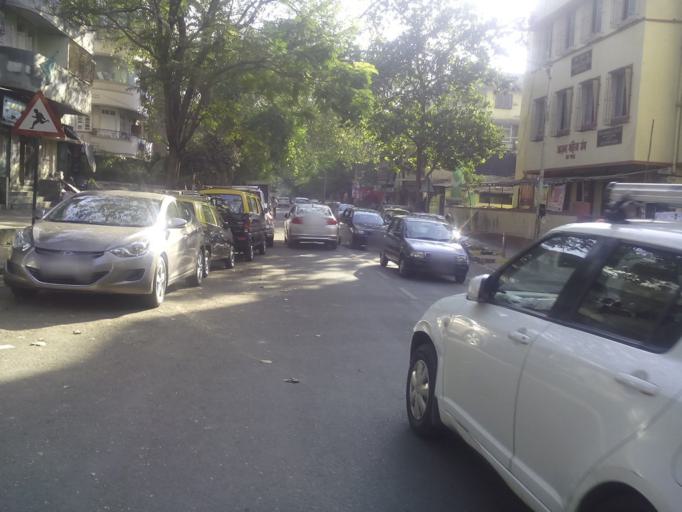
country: IN
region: Maharashtra
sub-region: Mumbai Suburban
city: Mumbai
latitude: 19.0423
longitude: 72.8628
